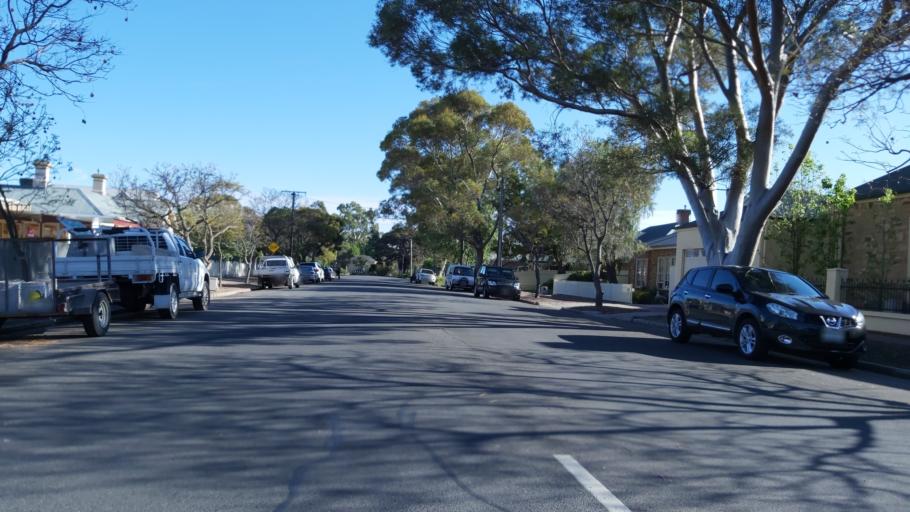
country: AU
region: South Australia
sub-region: Unley
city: Unley
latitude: -34.9491
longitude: 138.6117
